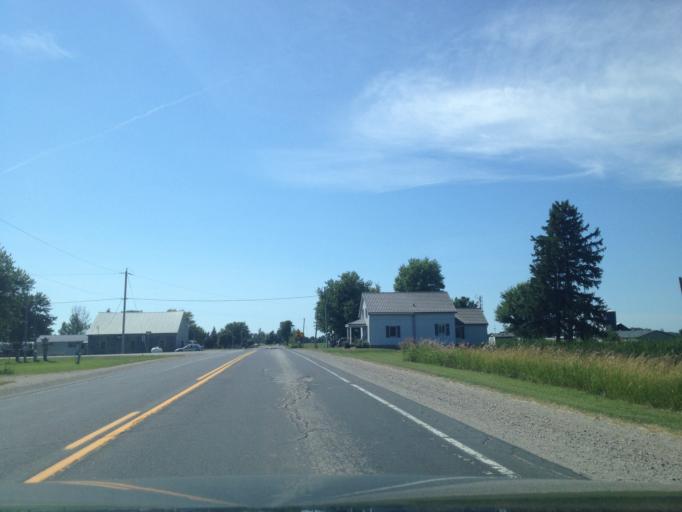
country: CA
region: Ontario
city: Stratford
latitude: 43.5010
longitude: -80.8761
